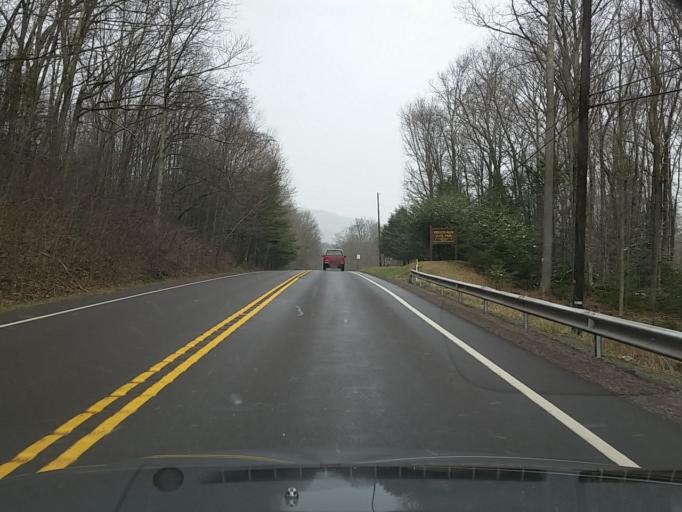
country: US
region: Pennsylvania
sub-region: Luzerne County
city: East Berwick
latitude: 41.2963
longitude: -76.2851
